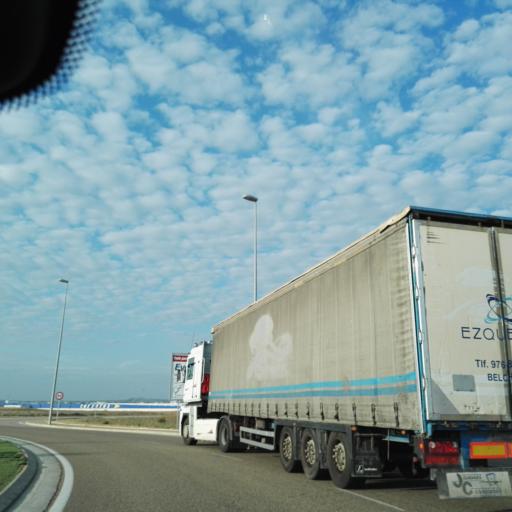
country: ES
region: Aragon
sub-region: Provincia de Zaragoza
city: Utebo
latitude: 41.6538
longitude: -1.0006
